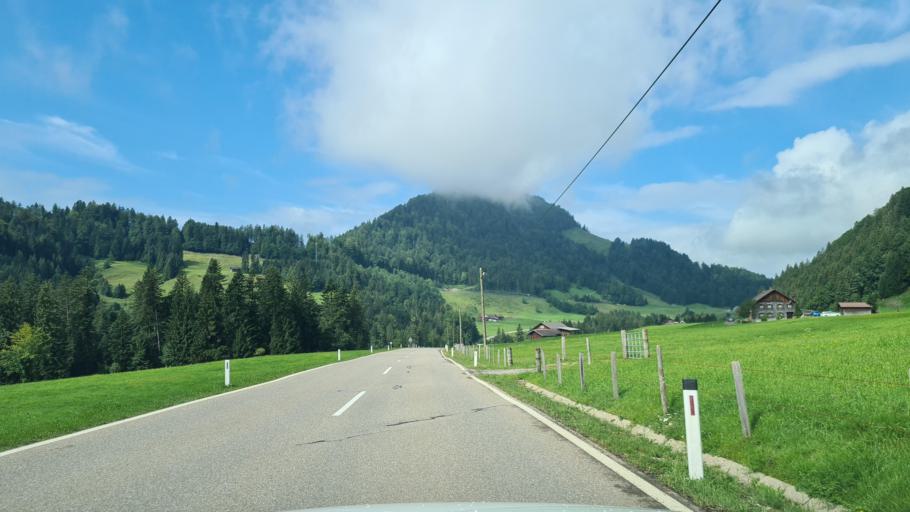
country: AT
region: Vorarlberg
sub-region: Politischer Bezirk Bregenz
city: Sibratsgfall
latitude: 47.4483
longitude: 10.0202
